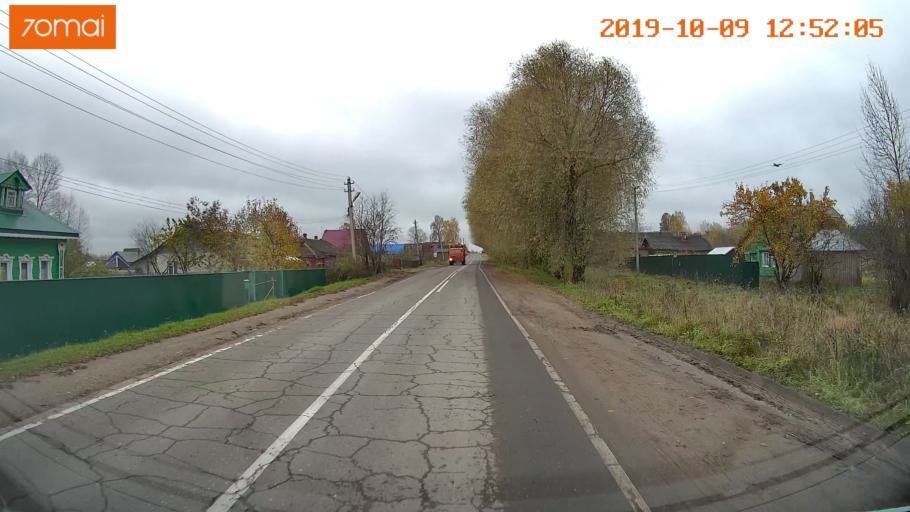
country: RU
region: Jaroslavl
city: Prechistoye
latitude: 58.4166
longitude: 40.3487
